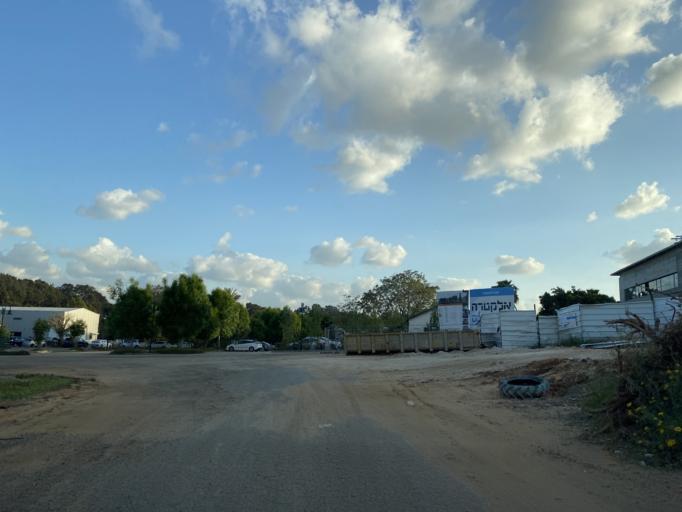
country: IL
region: Tel Aviv
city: Herzliyya
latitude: 32.1584
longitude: 34.8333
